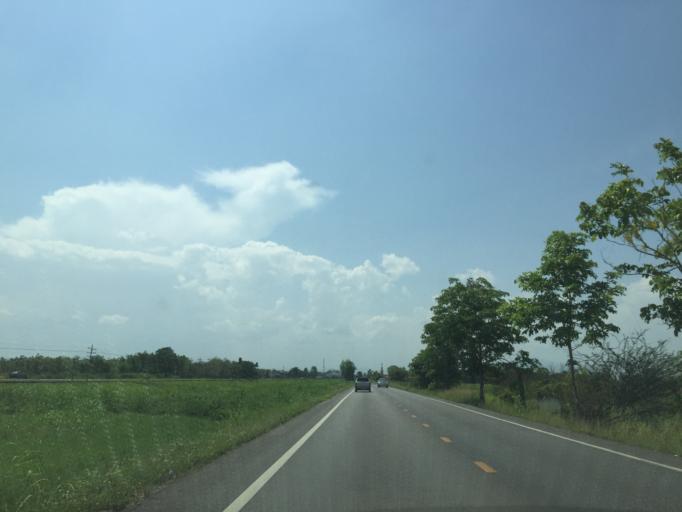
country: TH
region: Lamphun
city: Lamphun
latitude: 18.5698
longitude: 99.0323
